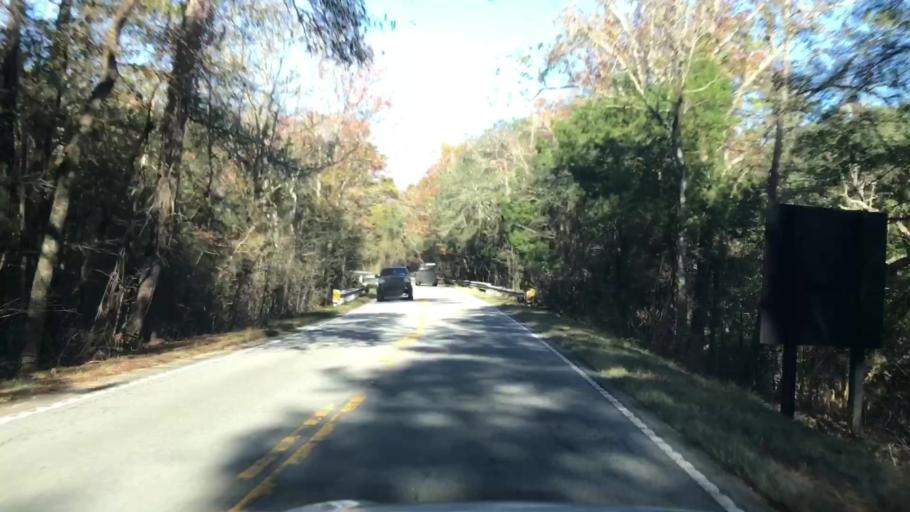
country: US
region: South Carolina
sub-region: Berkeley County
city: Ladson
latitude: 32.9094
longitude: -80.1490
